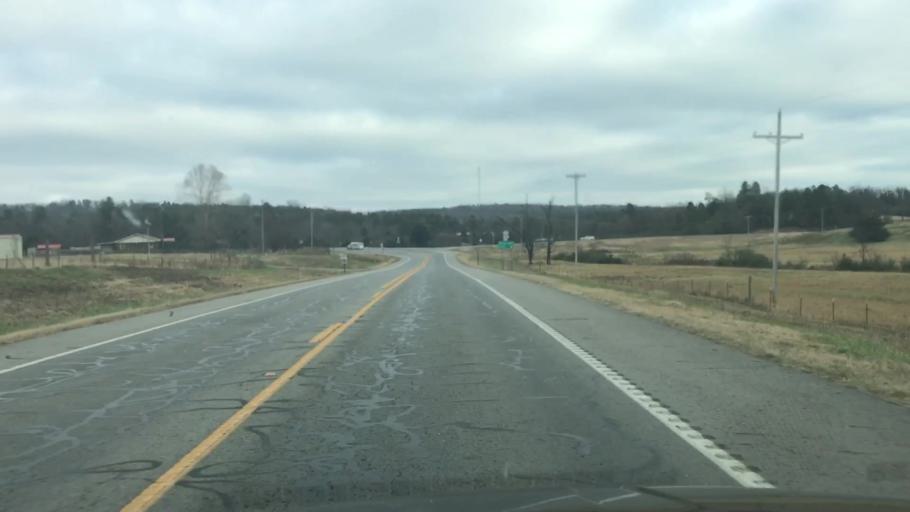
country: US
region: Arkansas
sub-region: Scott County
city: Waldron
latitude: 34.8060
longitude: -94.0401
